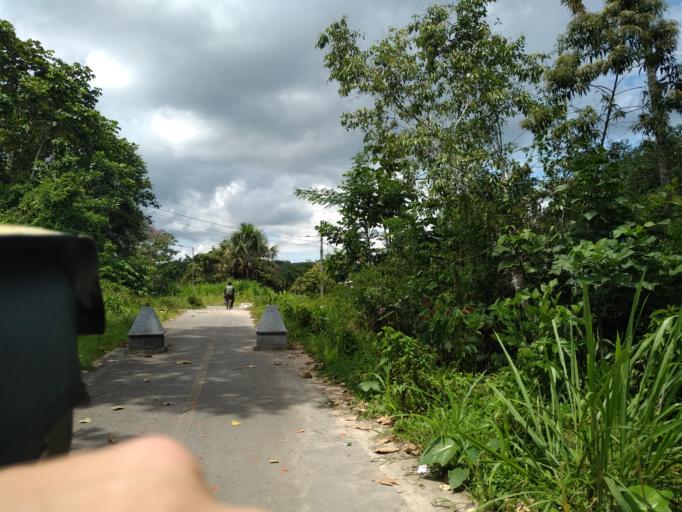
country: EC
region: Napo
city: Tena
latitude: -0.9892
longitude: -77.8224
